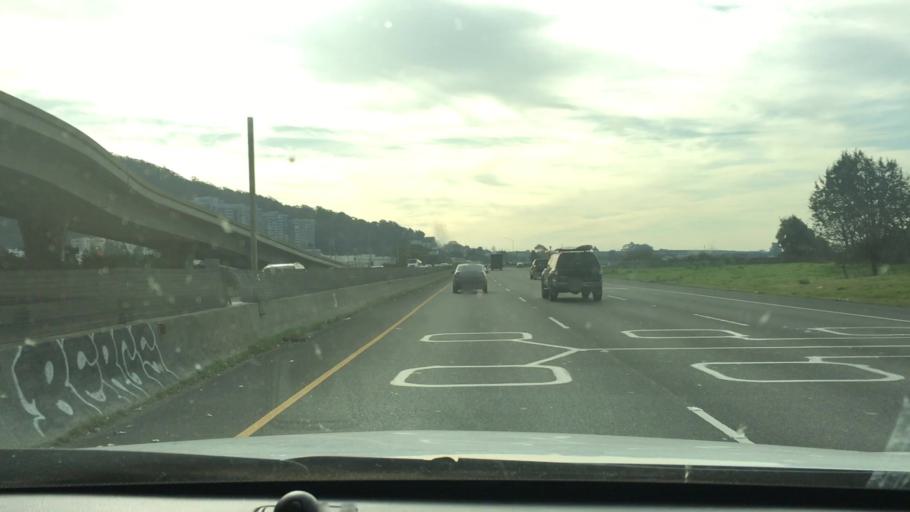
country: US
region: California
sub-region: Contra Costa County
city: El Cerrito
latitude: 37.8999
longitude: -122.3139
